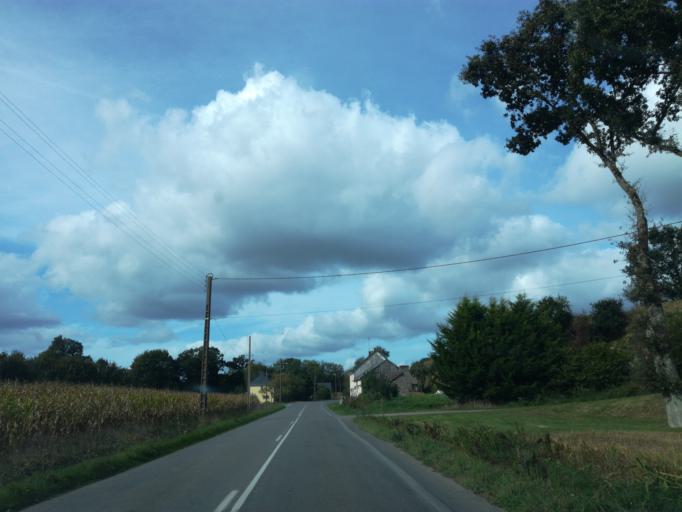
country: FR
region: Brittany
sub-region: Departement du Morbihan
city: Rohan
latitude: 48.0814
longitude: -2.7616
